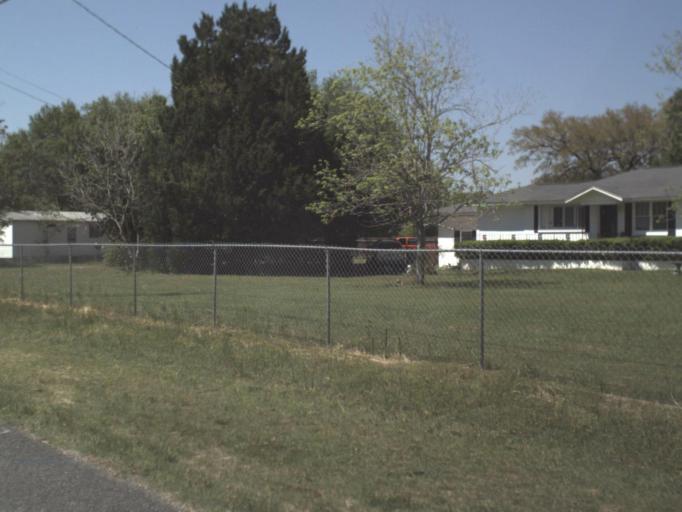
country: US
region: Florida
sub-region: Escambia County
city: Bellview
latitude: 30.5100
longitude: -87.3633
